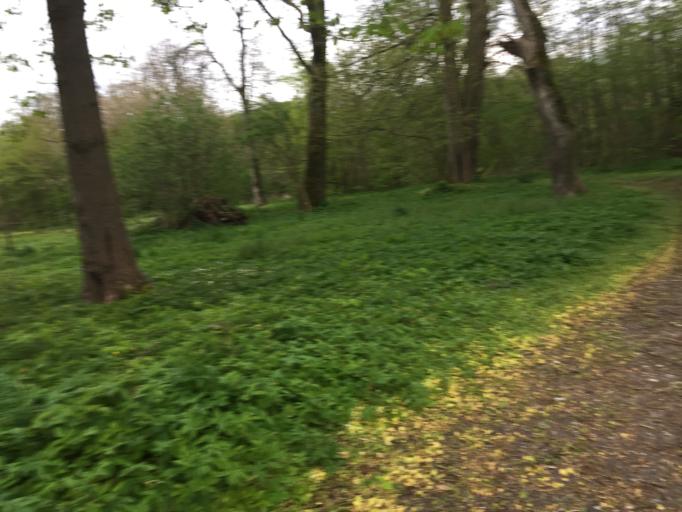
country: DK
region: North Denmark
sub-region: Alborg Kommune
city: Frejlev
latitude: 57.0031
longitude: 9.7748
